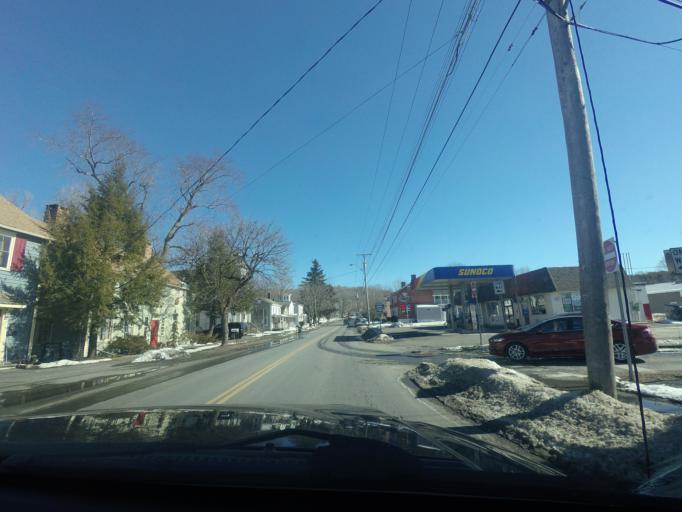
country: US
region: New York
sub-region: Rensselaer County
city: Nassau
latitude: 42.5161
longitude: -73.6097
